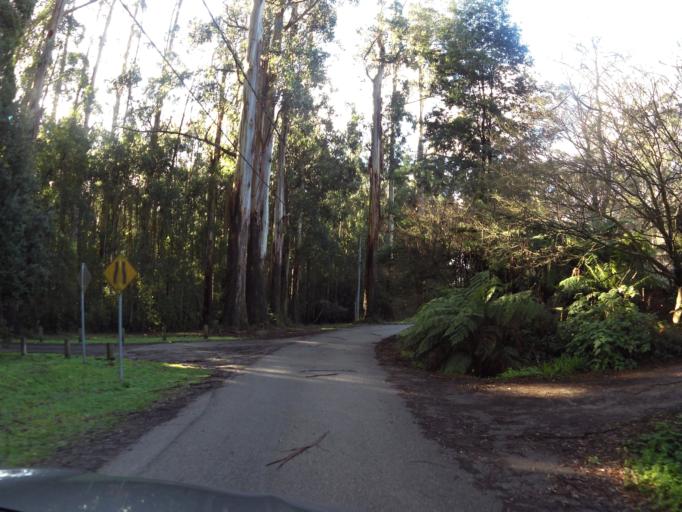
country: AU
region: Victoria
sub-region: Yarra Ranges
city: Kallista
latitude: -37.8842
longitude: 145.3584
